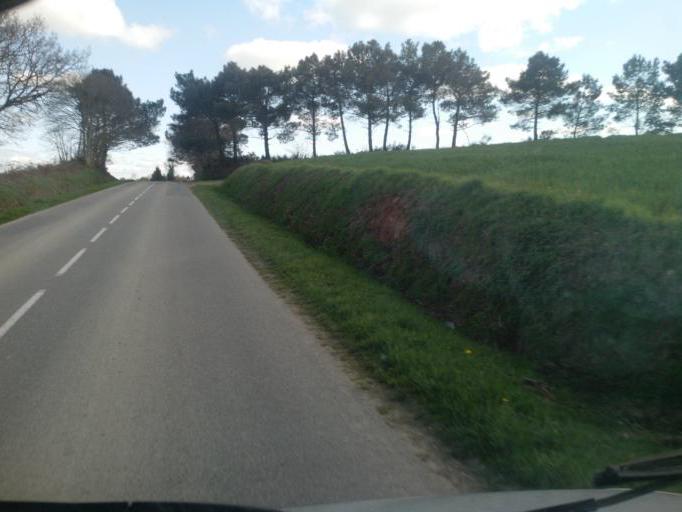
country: FR
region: Brittany
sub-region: Departement d'Ille-et-Vilaine
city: Maure-de-Bretagne
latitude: 47.9239
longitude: -1.9976
